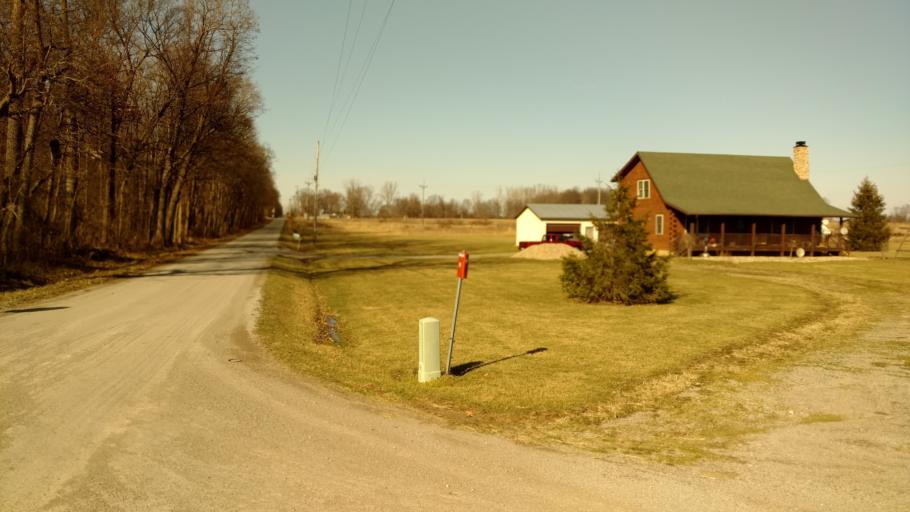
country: US
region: Ohio
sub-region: Wyandot County
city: Upper Sandusky
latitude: 40.7023
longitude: -83.2265
